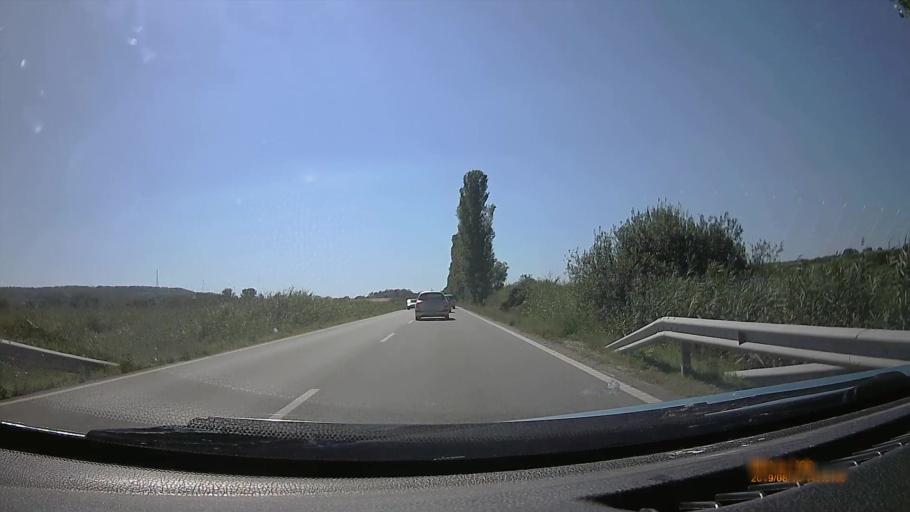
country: HU
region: Tolna
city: Simontornya
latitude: 46.7614
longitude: 18.5582
